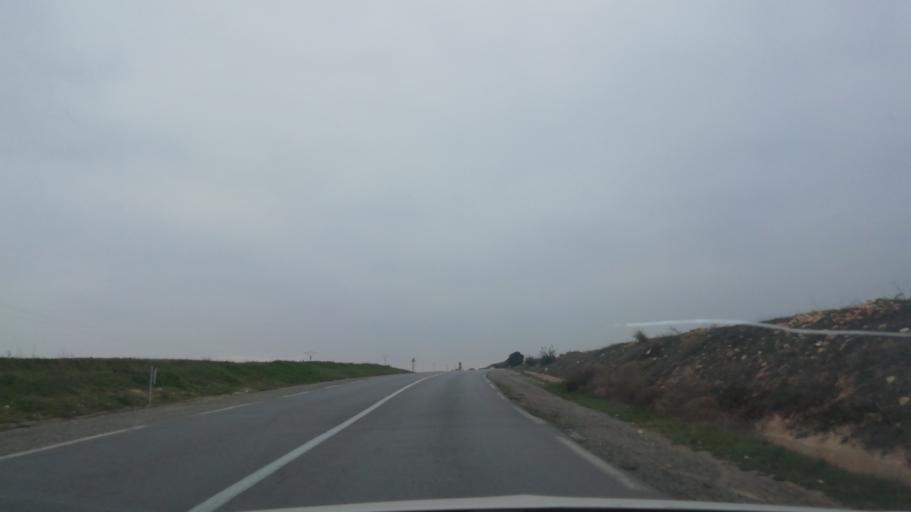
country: DZ
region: Sidi Bel Abbes
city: Sfizef
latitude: 35.2715
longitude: -0.1569
